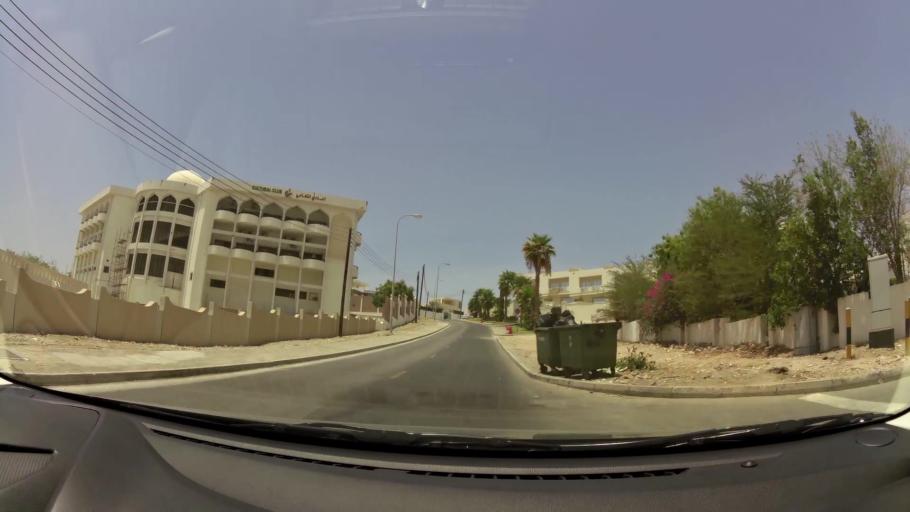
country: OM
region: Muhafazat Masqat
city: Muscat
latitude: 23.6244
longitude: 58.4926
